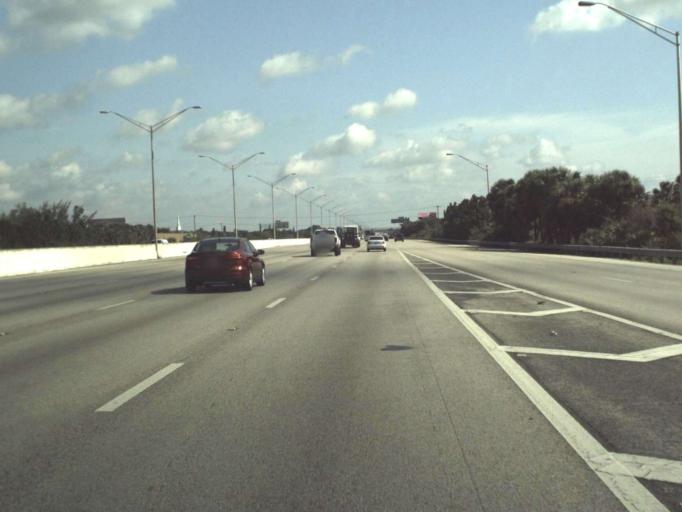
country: US
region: Florida
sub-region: Palm Beach County
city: North Palm Beach
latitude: 26.7872
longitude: -80.0988
